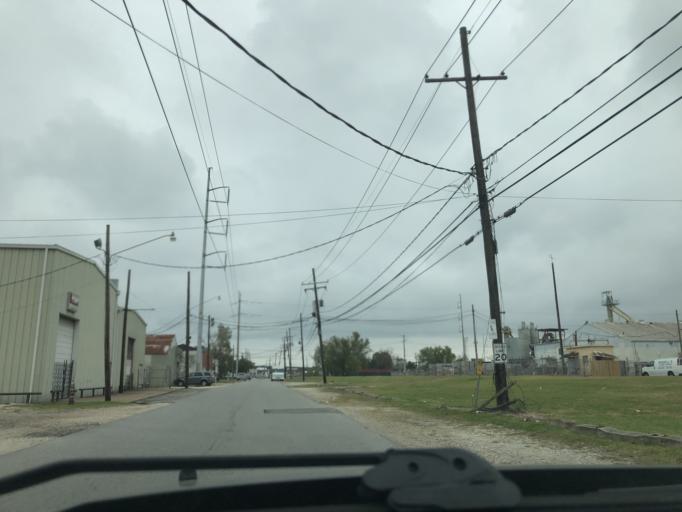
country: US
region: Louisiana
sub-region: Jefferson Parish
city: Metairie Terrace
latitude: 29.9745
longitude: -90.1640
